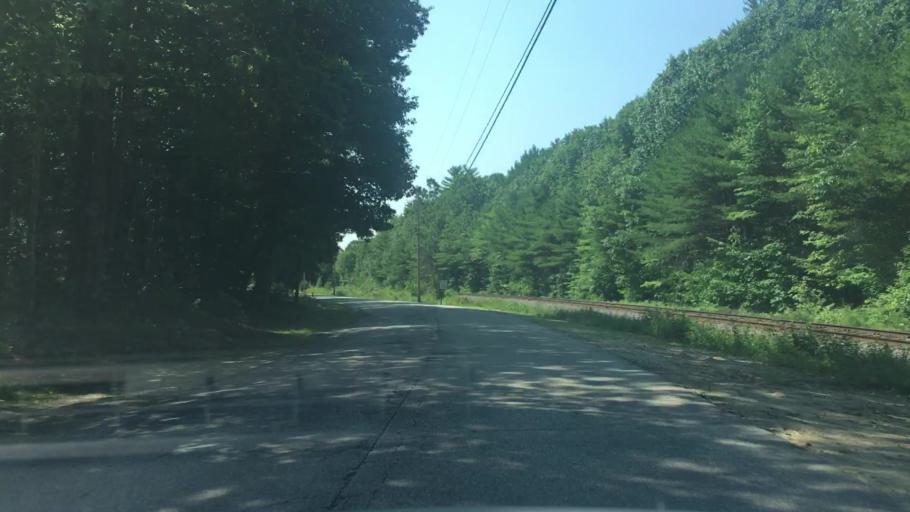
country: US
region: Maine
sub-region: Oxford County
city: South Paris
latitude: 44.1972
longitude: -70.5177
